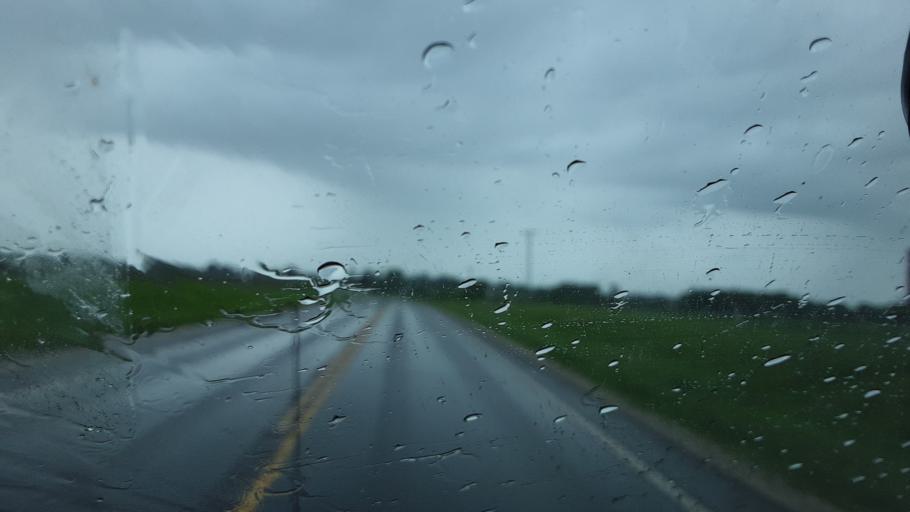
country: US
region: Missouri
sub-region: Monroe County
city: Paris
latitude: 39.4800
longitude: -92.1730
